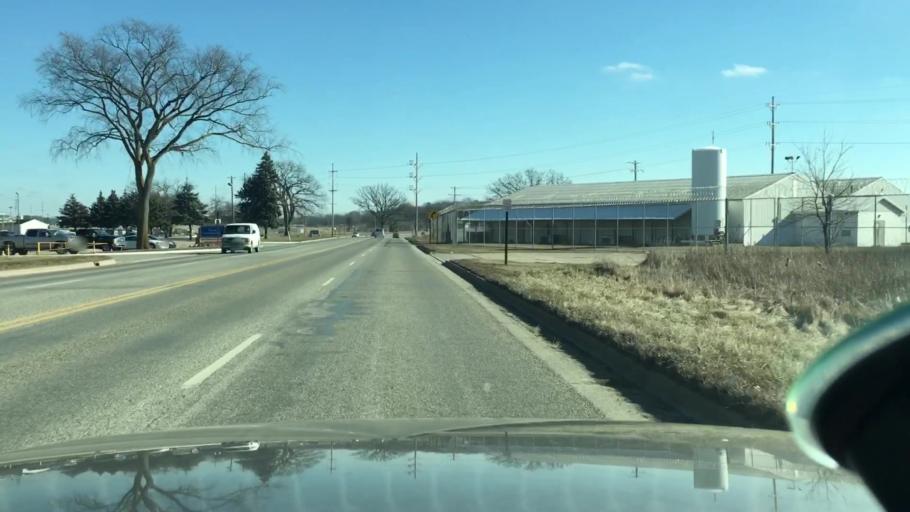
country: US
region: Michigan
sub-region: Jackson County
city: Jackson
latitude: 42.2911
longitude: -84.3924
